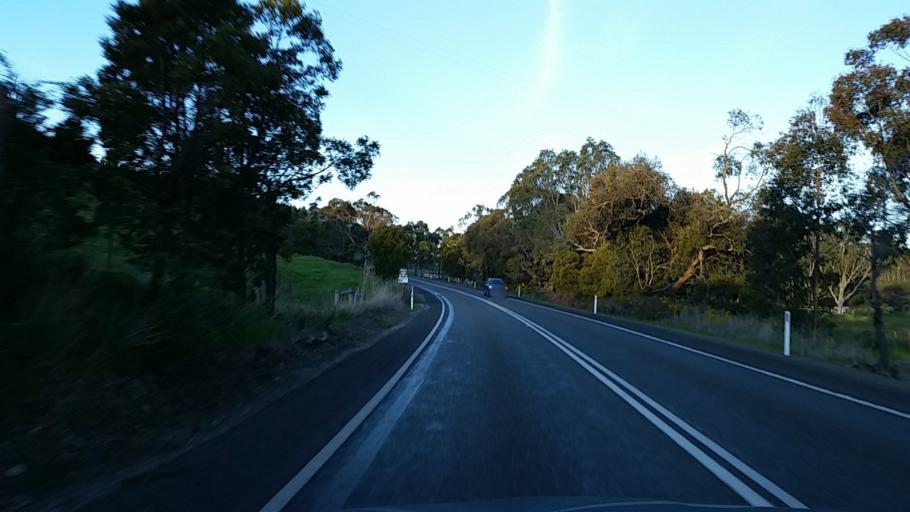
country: AU
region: South Australia
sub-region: Alexandrina
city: Mount Compass
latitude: -35.3178
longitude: 138.5651
